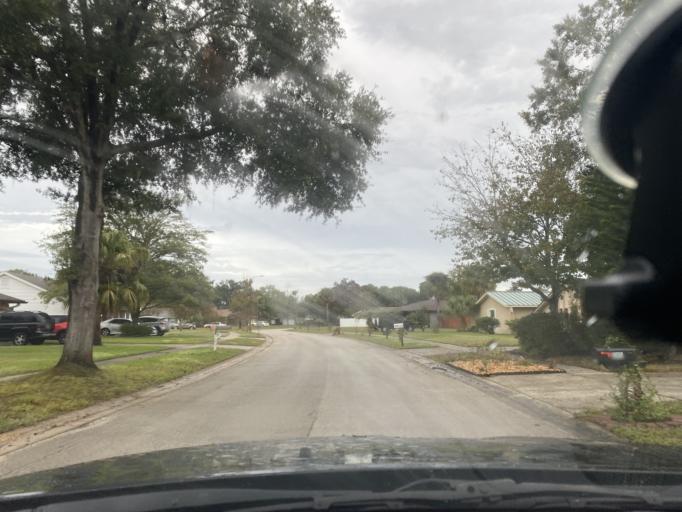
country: US
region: Florida
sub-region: Orange County
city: Azalea Park
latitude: 28.5372
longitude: -81.2631
